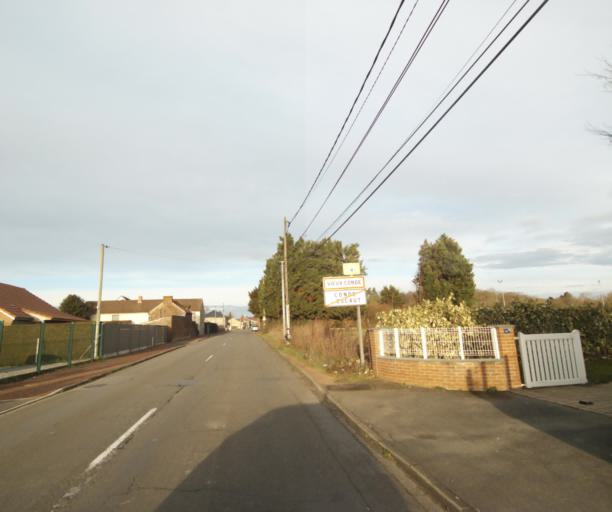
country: FR
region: Nord-Pas-de-Calais
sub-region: Departement du Nord
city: Conde-sur-l'Escaut
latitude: 50.4586
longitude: 3.5813
